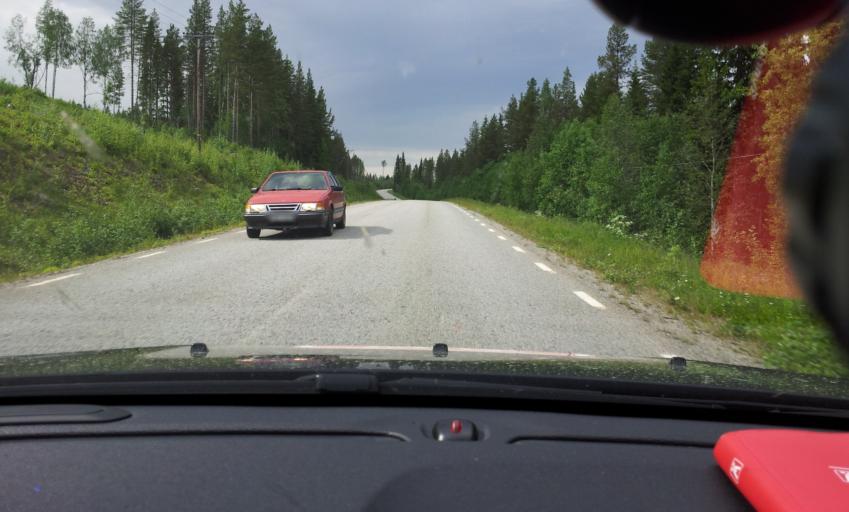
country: SE
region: Jaemtland
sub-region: Bergs Kommun
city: Hoverberg
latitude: 62.6660
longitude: 14.7293
